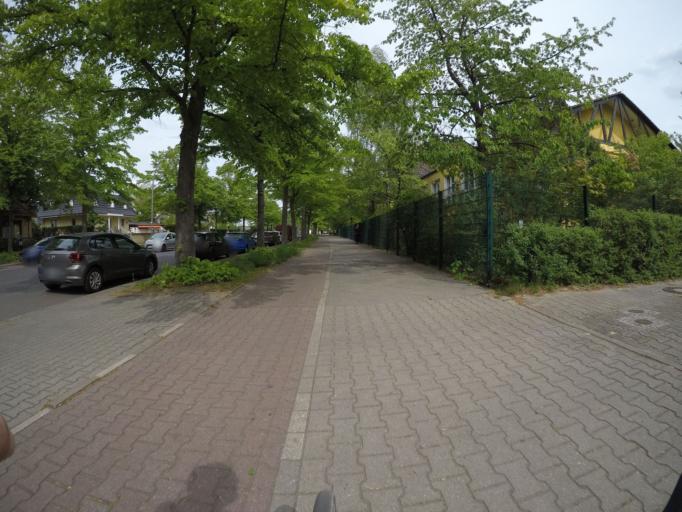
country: DE
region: Berlin
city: Altglienicke
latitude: 52.4201
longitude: 13.5141
